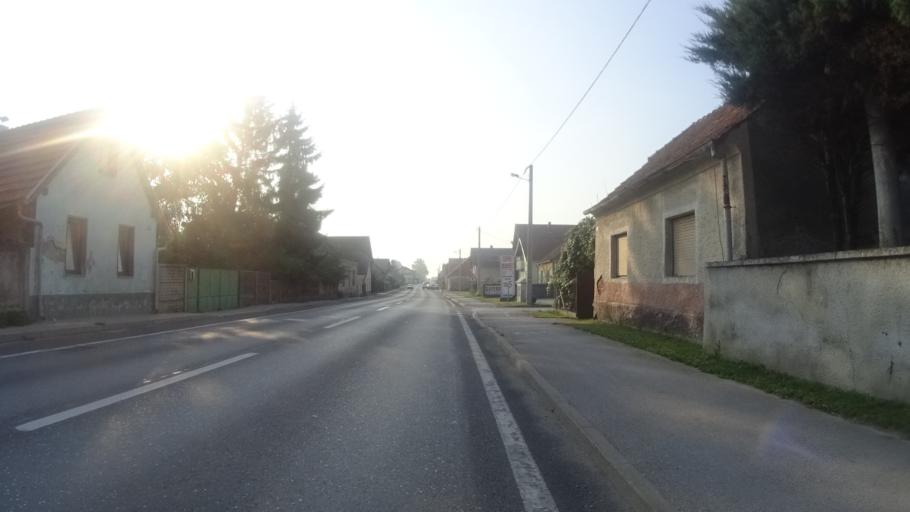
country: HR
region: Varazdinska
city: Petrijanec
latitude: 46.3457
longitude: 16.2280
